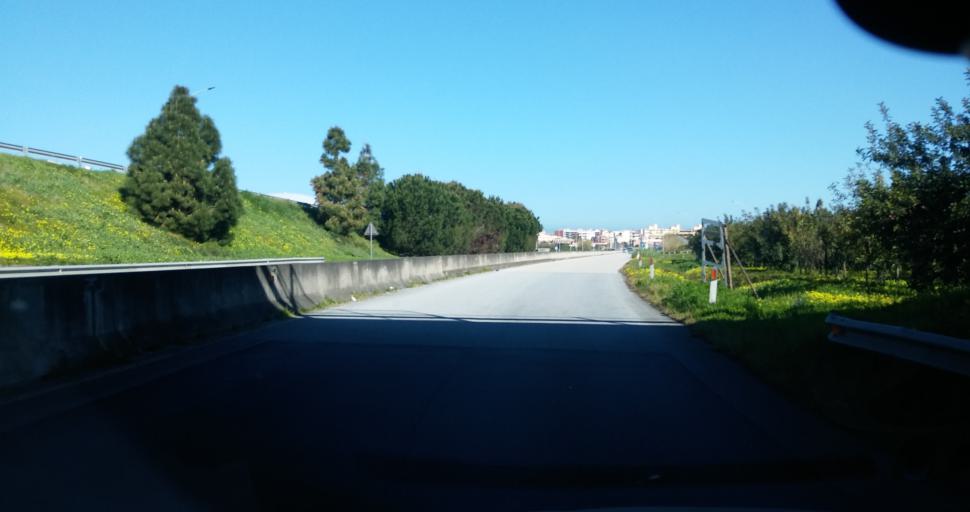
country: IT
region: Sicily
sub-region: Messina
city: Milazzo
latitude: 38.2072
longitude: 15.2381
